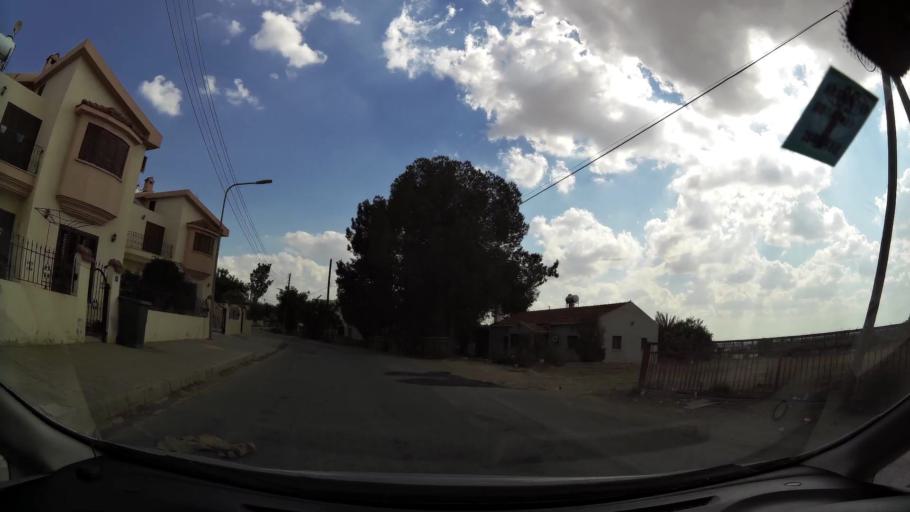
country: CY
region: Lefkosia
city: Nicosia
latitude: 35.2072
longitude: 33.3825
